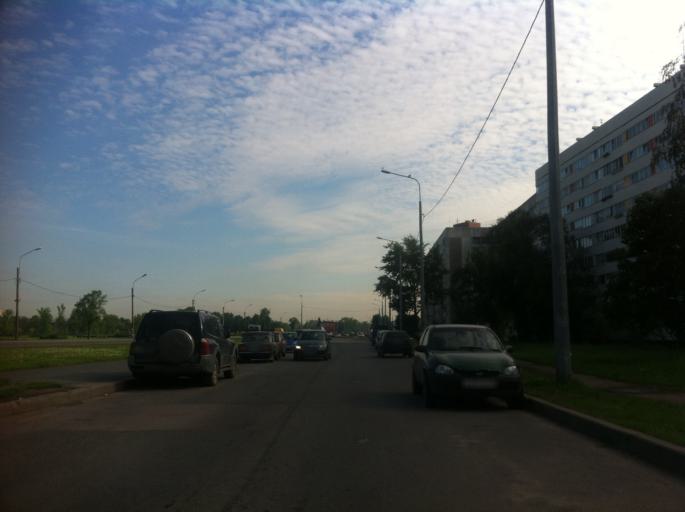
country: RU
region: St.-Petersburg
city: Uritsk
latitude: 59.8290
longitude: 30.1907
